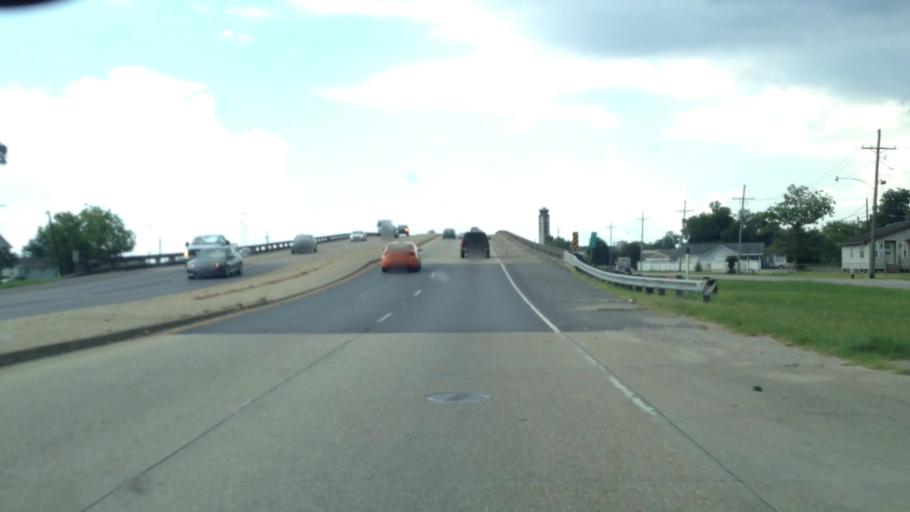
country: US
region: Louisiana
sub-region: Jefferson Parish
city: Kenner
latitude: 29.9820
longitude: -90.2696
